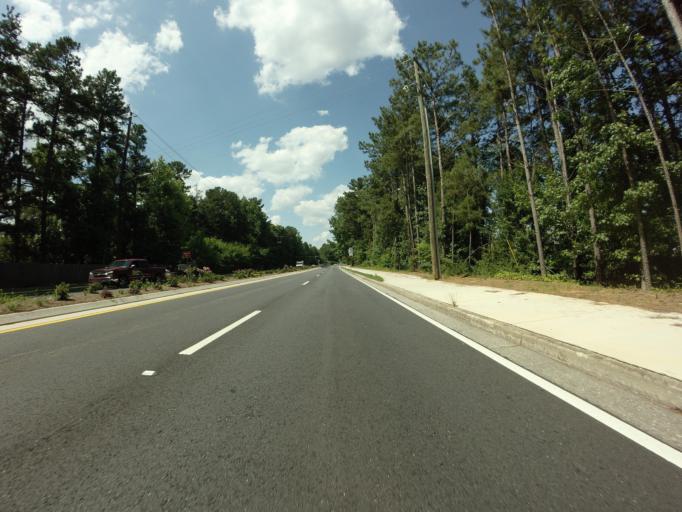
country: US
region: Georgia
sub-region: Fulton County
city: Johns Creek
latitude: 34.0560
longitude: -84.2175
